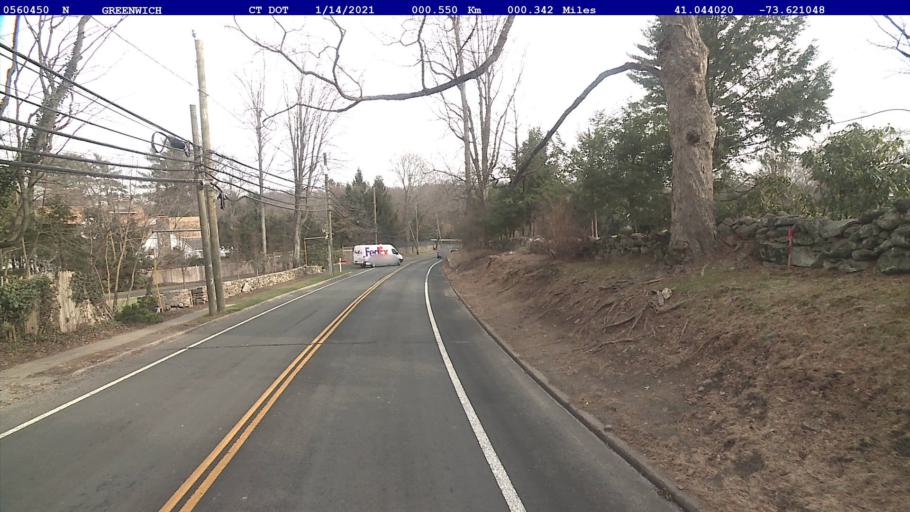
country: US
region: Connecticut
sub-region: Fairfield County
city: Greenwich
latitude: 41.0440
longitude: -73.6210
